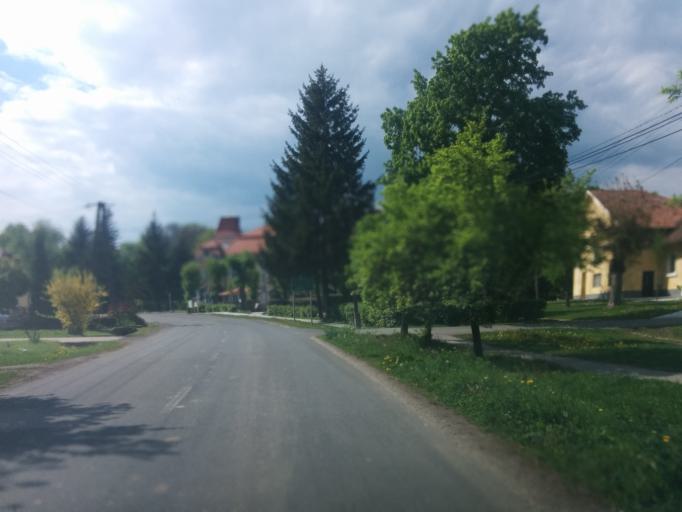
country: HU
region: Nograd
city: Romhany
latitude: 47.8456
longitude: 19.2947
